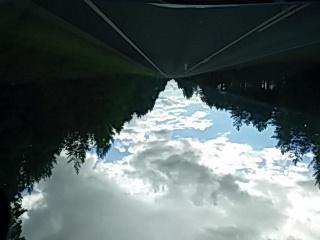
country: FI
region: Haeme
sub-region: Haemeenlinna
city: Renko
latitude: 60.8653
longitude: 24.1939
